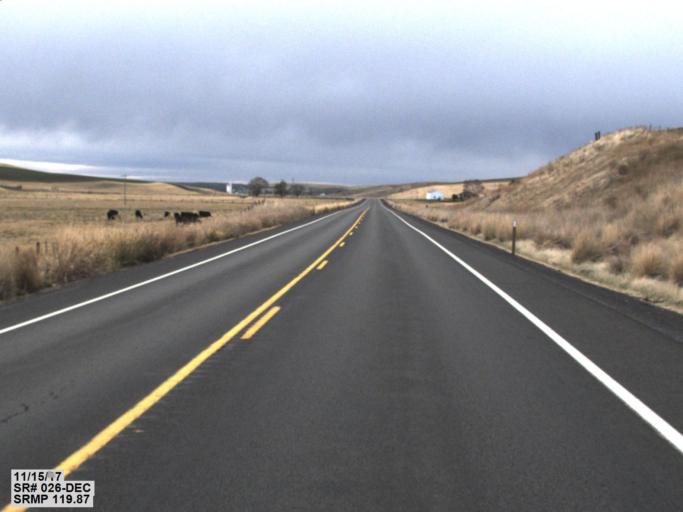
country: US
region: Washington
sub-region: Whitman County
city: Colfax
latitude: 46.8133
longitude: -117.5938
